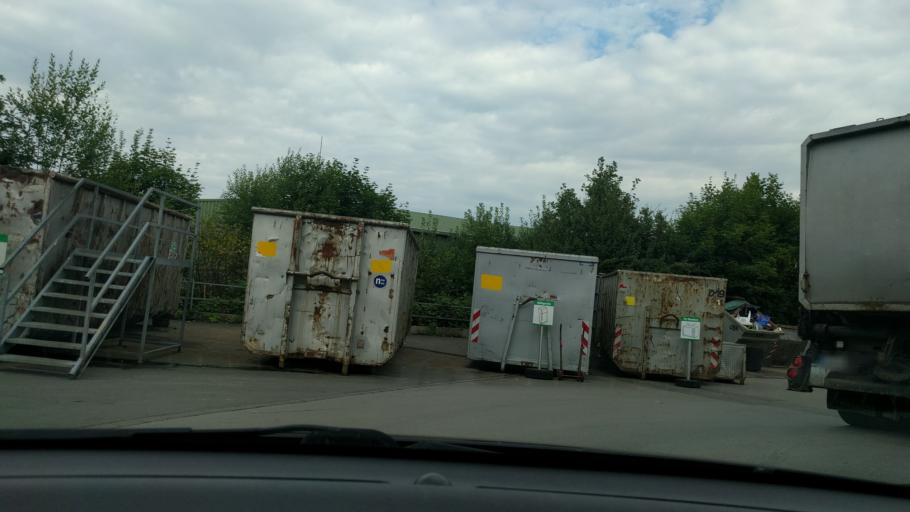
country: DE
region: North Rhine-Westphalia
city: Witten
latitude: 51.4594
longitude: 7.3482
